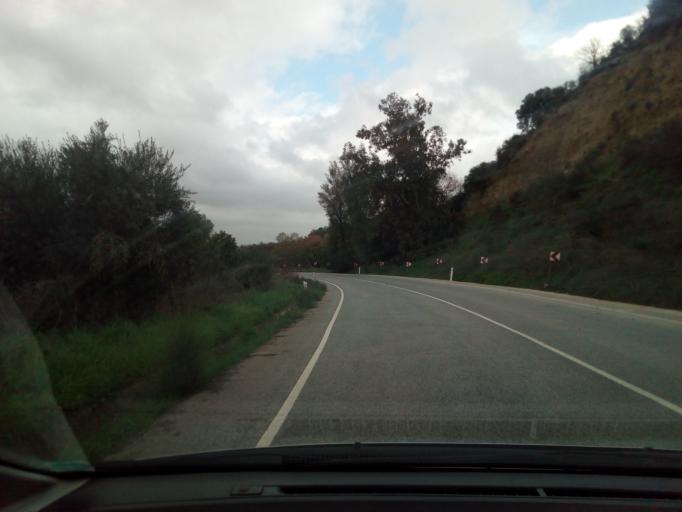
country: CY
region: Pafos
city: Polis
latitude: 34.9431
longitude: 32.4702
